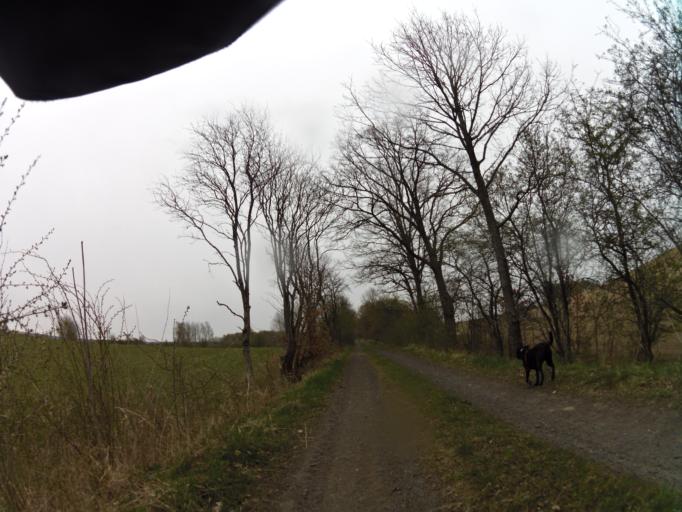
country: PL
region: West Pomeranian Voivodeship
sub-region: Powiat koszalinski
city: Bobolice
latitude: 53.9865
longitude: 16.6589
